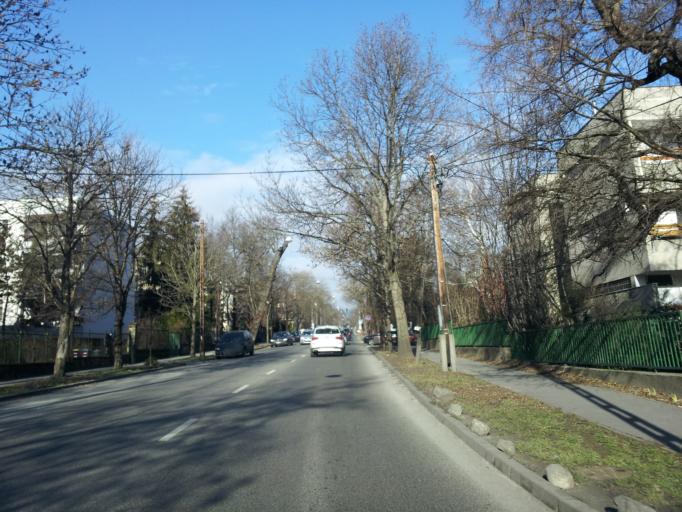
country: HU
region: Budapest
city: Budapest XII. keruelet
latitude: 47.5271
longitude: 18.9827
